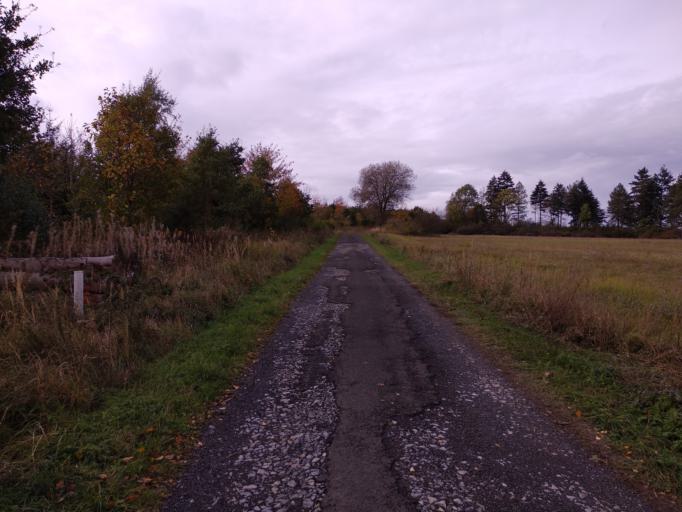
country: DE
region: North Rhine-Westphalia
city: Beverungen
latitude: 51.6701
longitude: 9.3382
